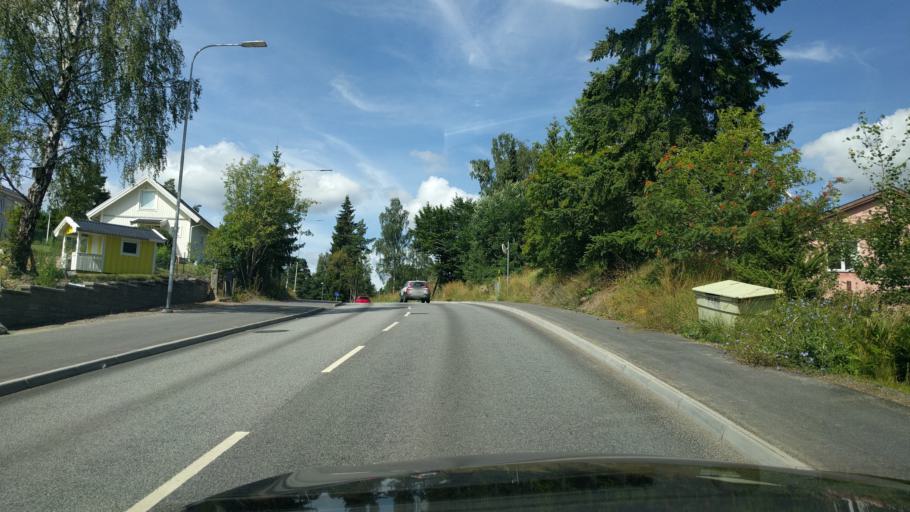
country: SE
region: Stockholm
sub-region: Taby Kommun
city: Taby
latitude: 59.4497
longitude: 18.0616
